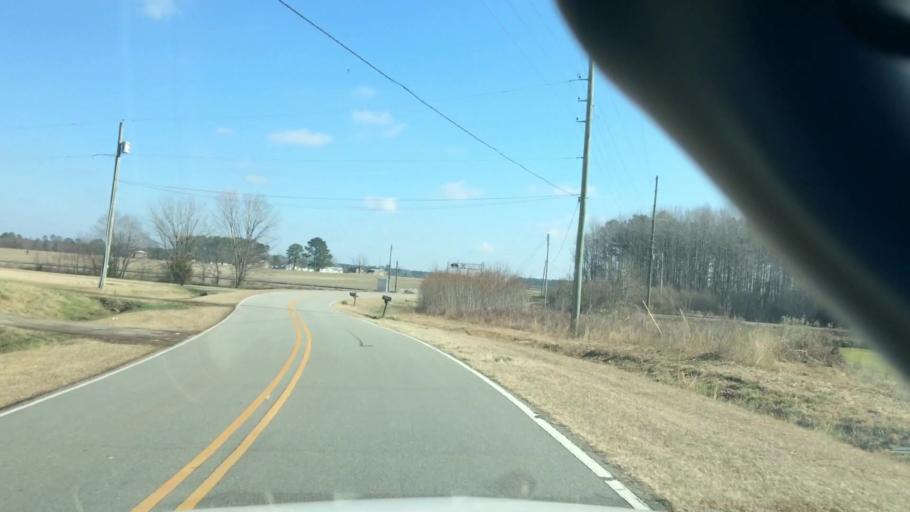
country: US
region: North Carolina
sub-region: Pitt County
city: Grifton
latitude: 35.4190
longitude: -77.4263
